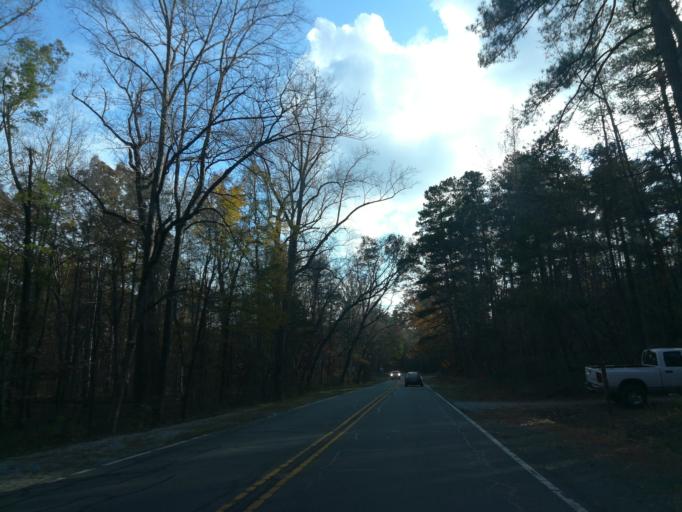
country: US
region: North Carolina
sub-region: Durham County
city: Durham
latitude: 36.0267
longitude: -78.9892
